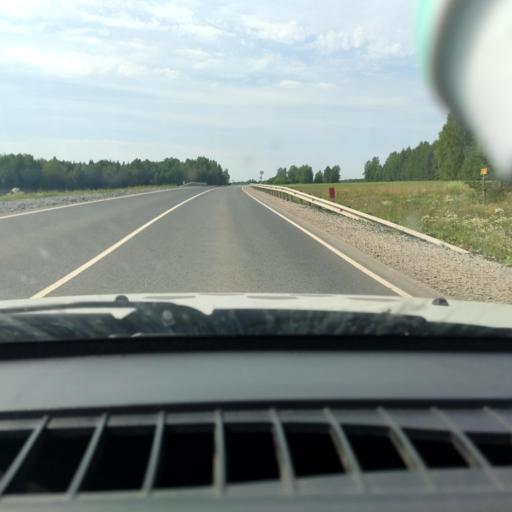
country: RU
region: Perm
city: Siva
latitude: 58.4870
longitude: 54.1327
